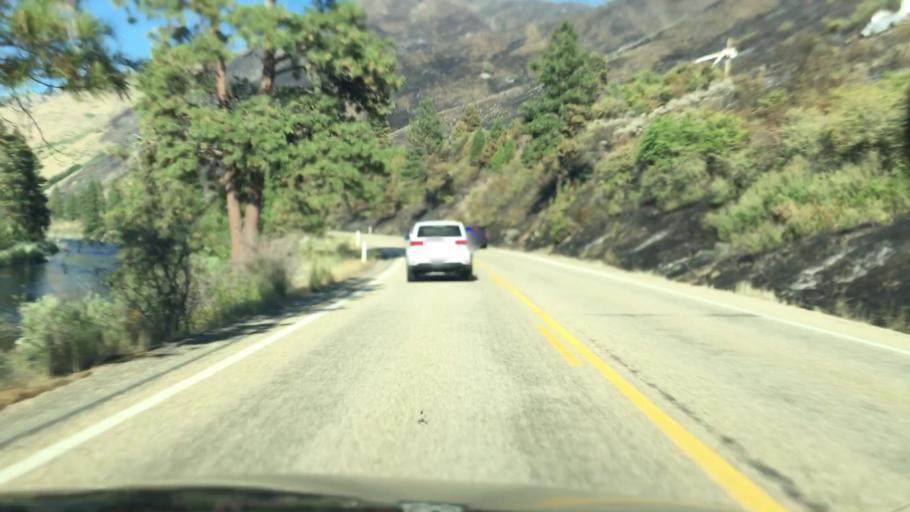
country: US
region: Idaho
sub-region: Gem County
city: Emmett
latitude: 44.0081
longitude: -116.1685
